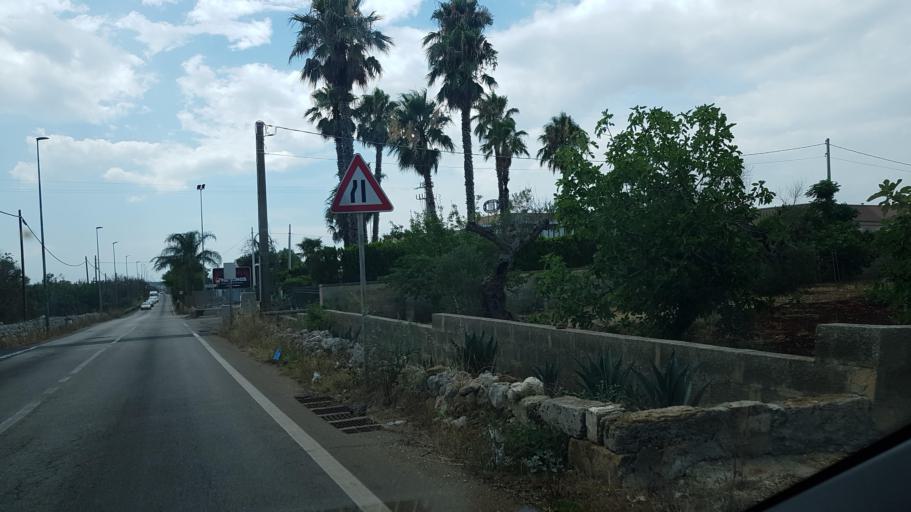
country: IT
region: Apulia
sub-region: Provincia di Lecce
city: Taurisano
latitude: 39.9591
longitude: 18.2289
